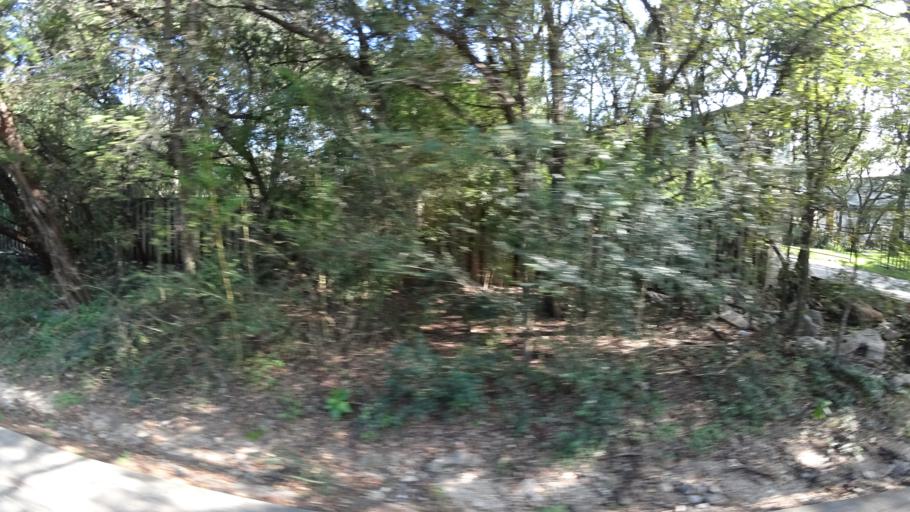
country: US
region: Texas
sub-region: Travis County
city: West Lake Hills
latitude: 30.2853
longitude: -97.8058
